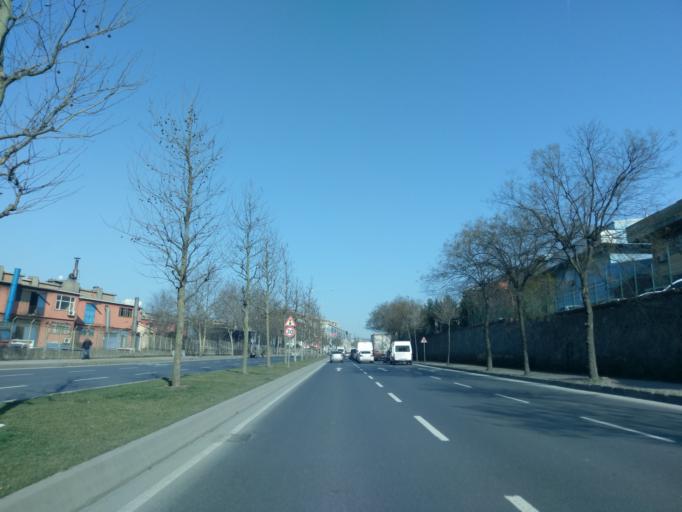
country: TR
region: Istanbul
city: Basaksehir
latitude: 41.0906
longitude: 28.7953
